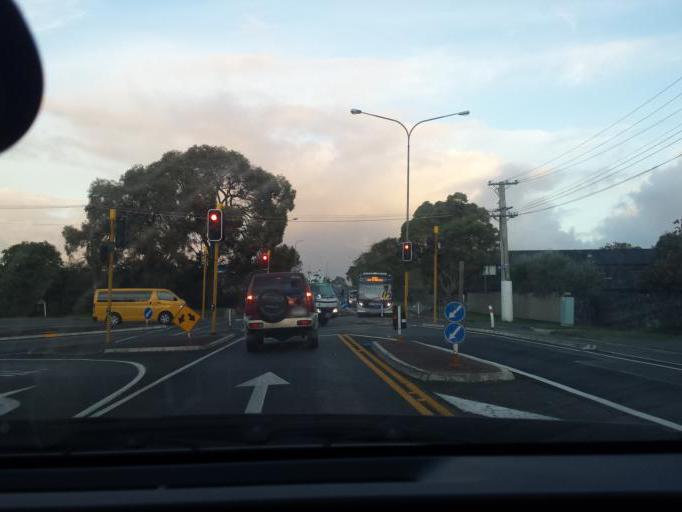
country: NZ
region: Auckland
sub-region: Auckland
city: Tamaki
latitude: -36.8679
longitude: 174.8486
